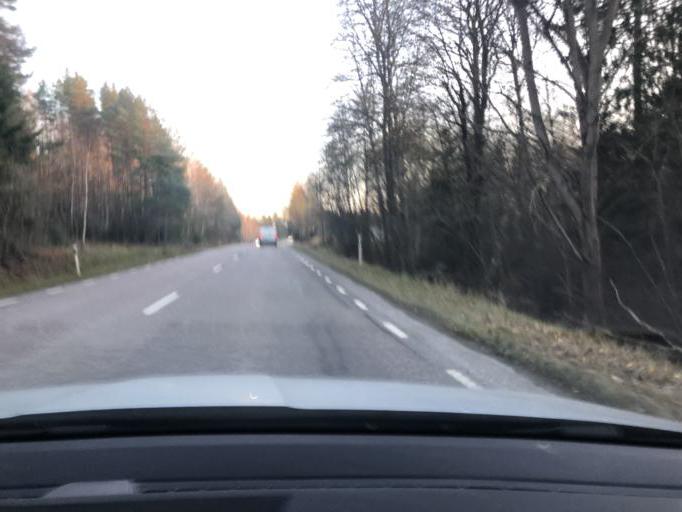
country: SE
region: Soedermanland
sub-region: Strangnas Kommun
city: Akers Styckebruk
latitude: 59.3049
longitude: 17.0947
